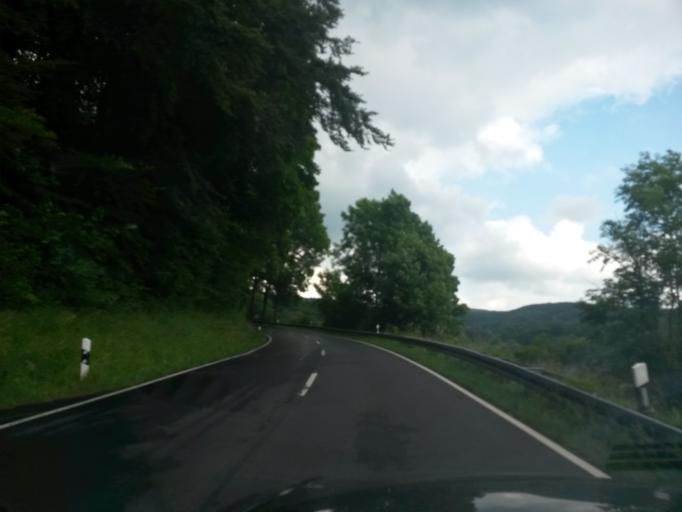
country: DE
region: Hesse
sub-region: Regierungsbezirk Kassel
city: Gersfeld
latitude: 50.4722
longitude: 9.9414
